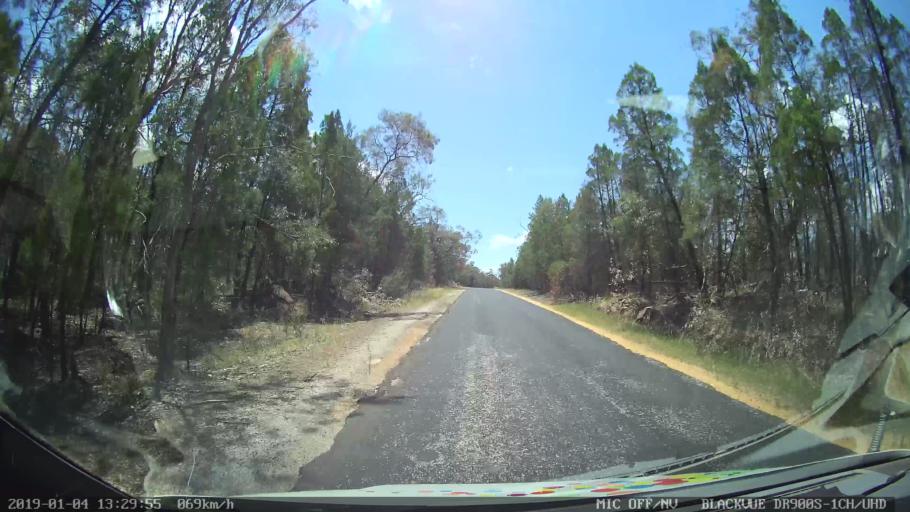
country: AU
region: New South Wales
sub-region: Parkes
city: Peak Hill
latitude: -32.6413
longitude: 148.5501
